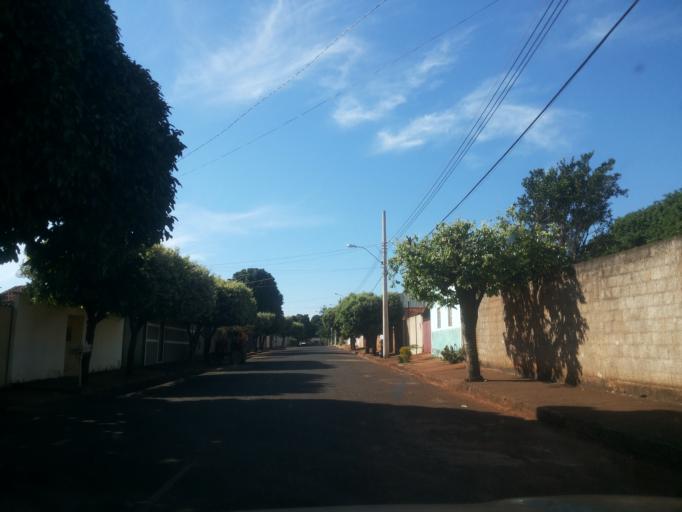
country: BR
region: Minas Gerais
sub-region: Centralina
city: Centralina
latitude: -18.7197
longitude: -49.2010
